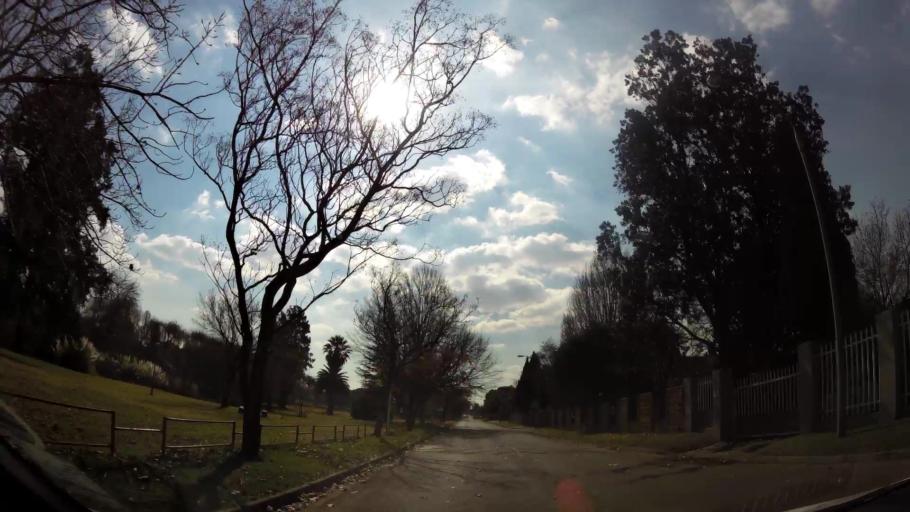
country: ZA
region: Gauteng
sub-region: Ekurhuleni Metropolitan Municipality
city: Germiston
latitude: -26.1866
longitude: 28.2024
